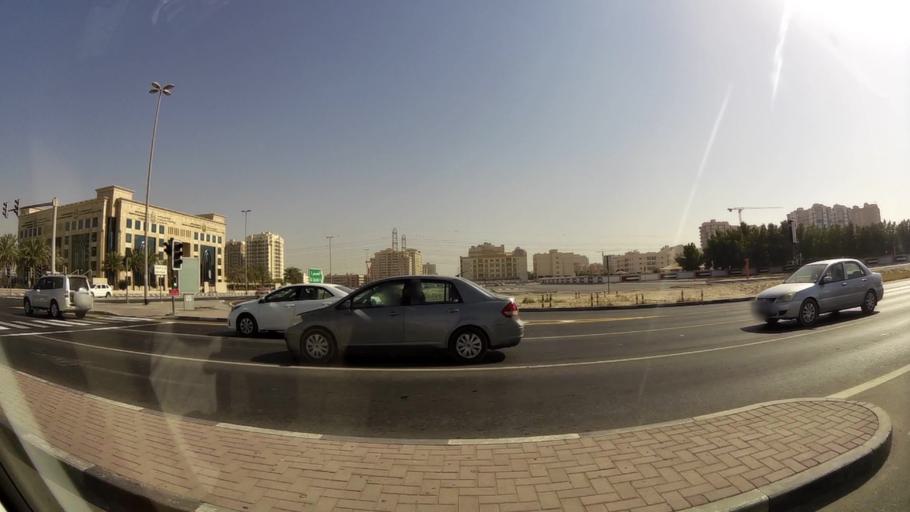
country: AE
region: Ash Shariqah
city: Sharjah
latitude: 25.2818
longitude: 55.3778
